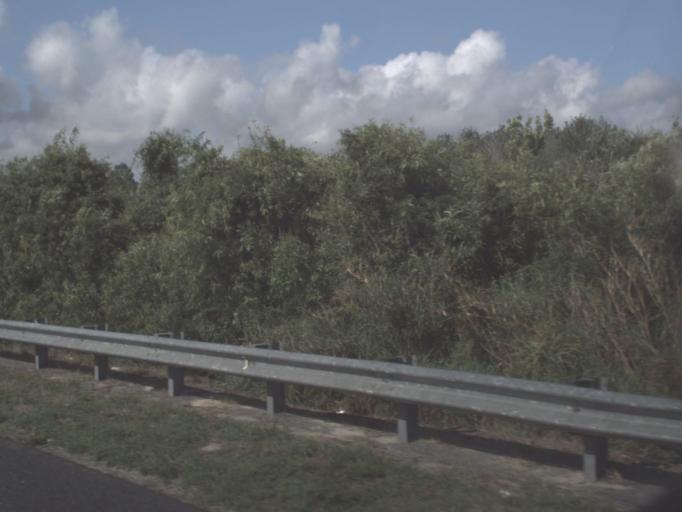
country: US
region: Florida
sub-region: Lake County
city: Leesburg
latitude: 28.7875
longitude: -81.8878
